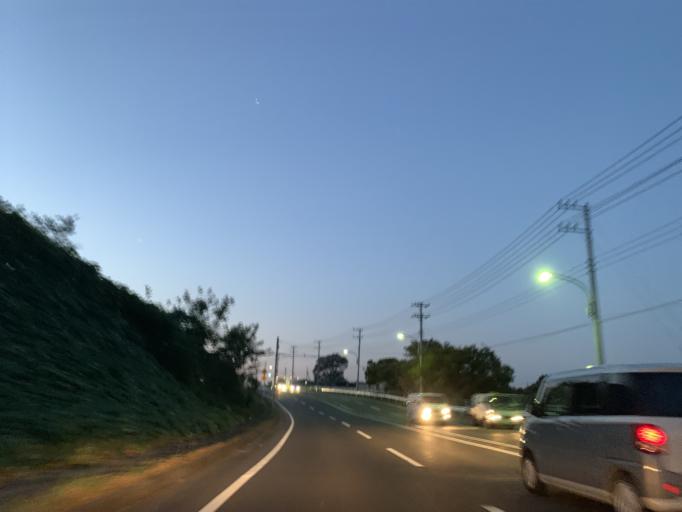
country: JP
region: Chiba
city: Nagareyama
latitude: 35.8749
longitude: 139.9070
